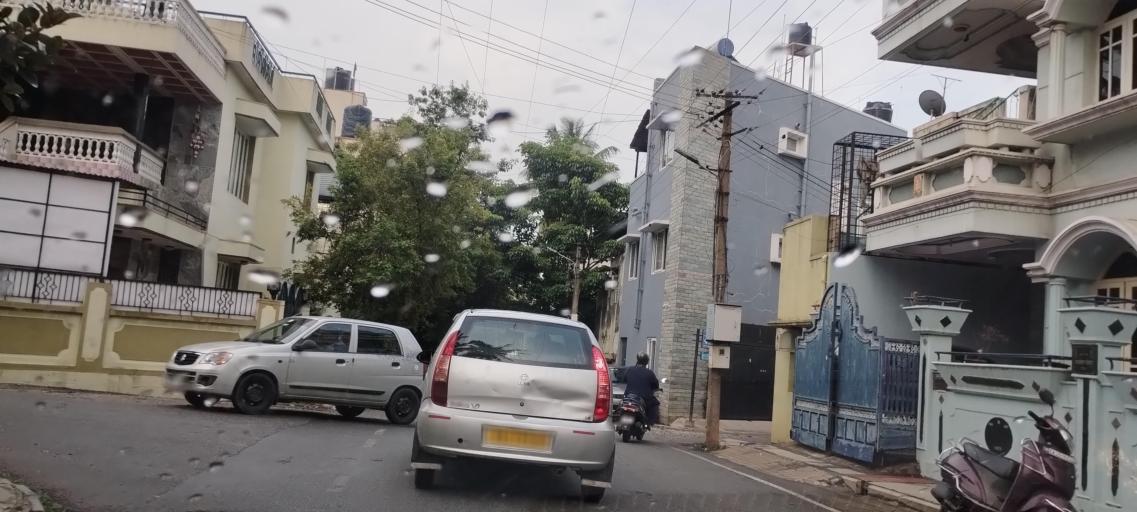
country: IN
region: Karnataka
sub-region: Bangalore Urban
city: Bangalore
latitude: 12.9392
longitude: 77.5626
